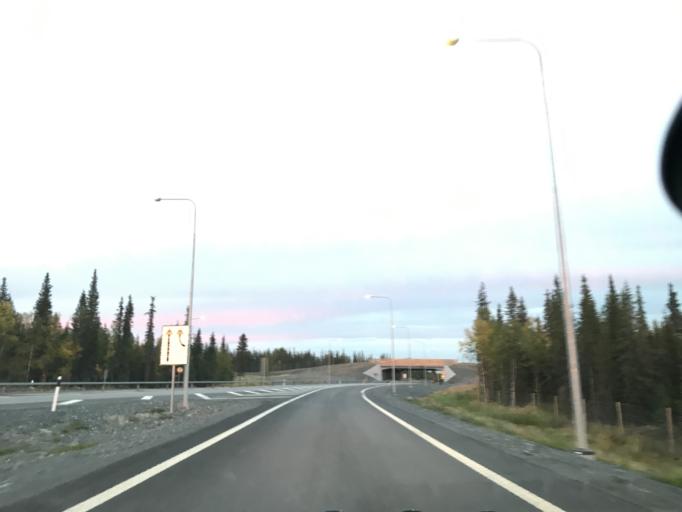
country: SE
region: Norrbotten
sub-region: Gallivare Kommun
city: Malmberget
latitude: 67.6944
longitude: 20.8084
